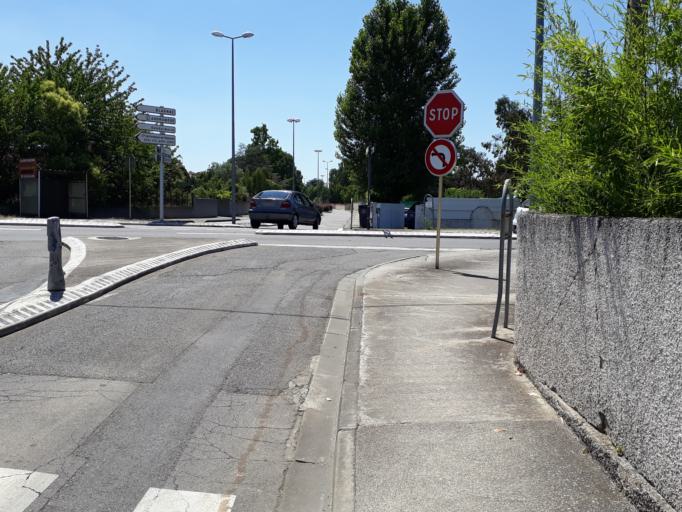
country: FR
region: Midi-Pyrenees
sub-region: Departement de la Haute-Garonne
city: Beauzelle
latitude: 43.6665
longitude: 1.3707
